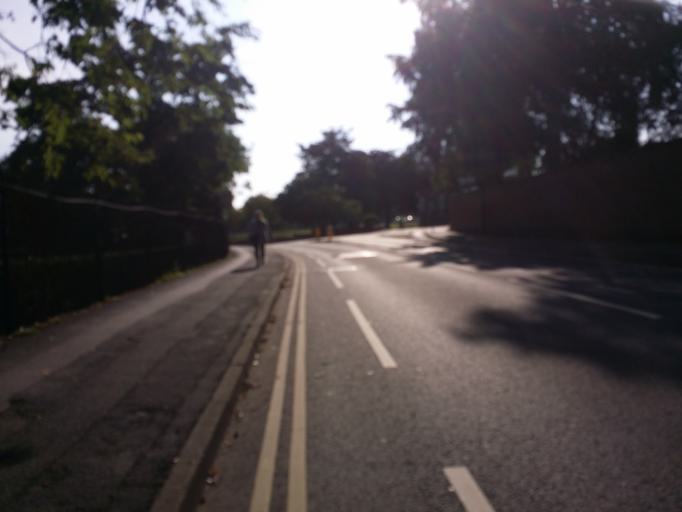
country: GB
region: England
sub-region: City of York
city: Heslington
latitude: 53.9520
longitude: -1.0637
